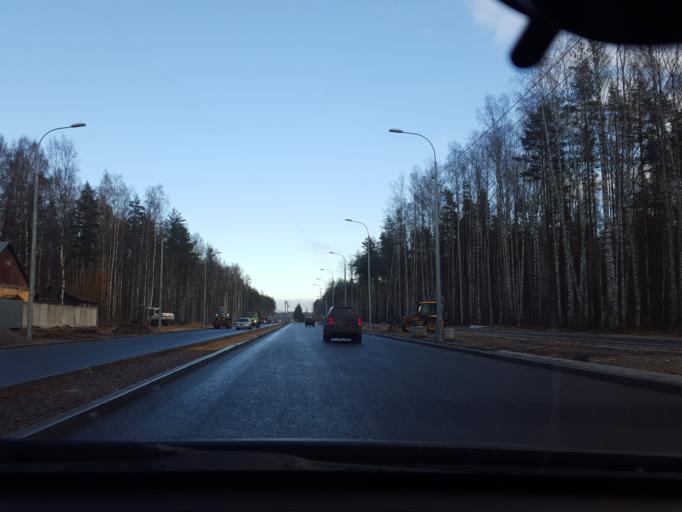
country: RU
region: St.-Petersburg
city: Pargolovo
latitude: 60.0588
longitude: 30.2448
